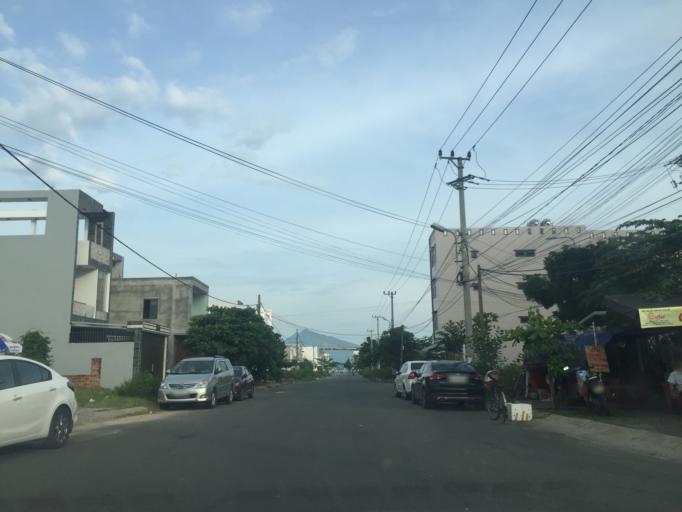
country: VN
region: Da Nang
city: Da Nang
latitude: 16.0920
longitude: 108.2280
